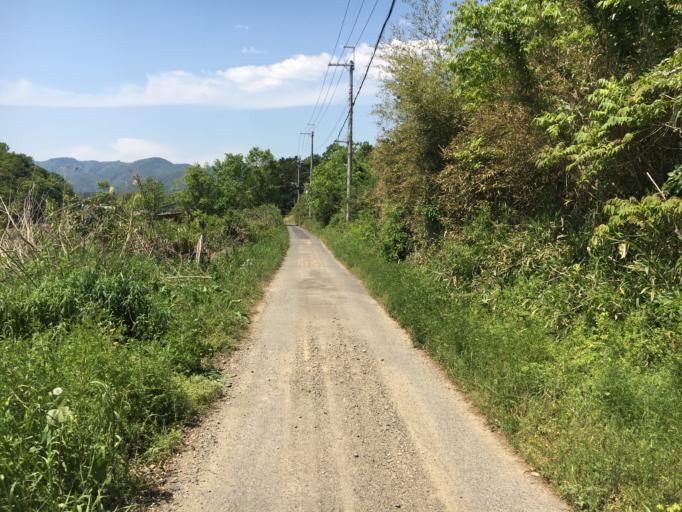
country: JP
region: Kyoto
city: Kameoka
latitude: 35.0698
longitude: 135.5700
